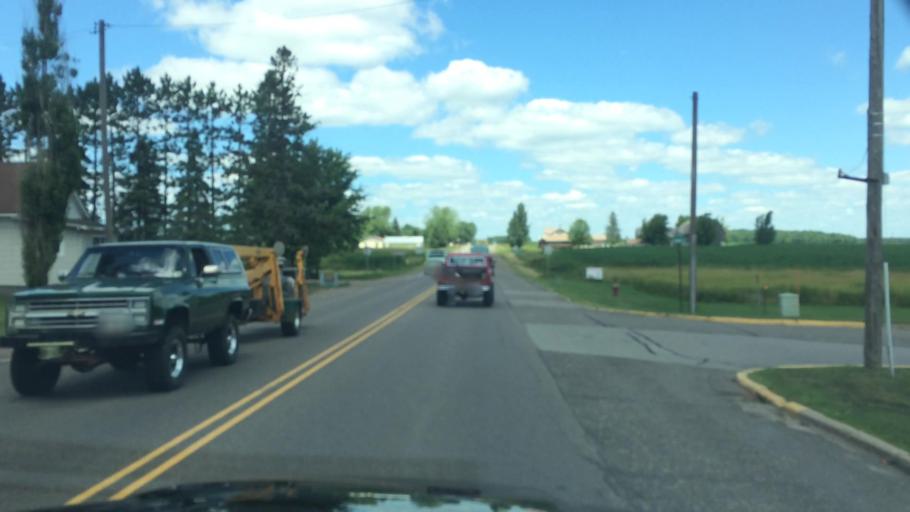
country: US
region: Wisconsin
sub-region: Taylor County
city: Medford
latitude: 45.0803
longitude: -90.3147
